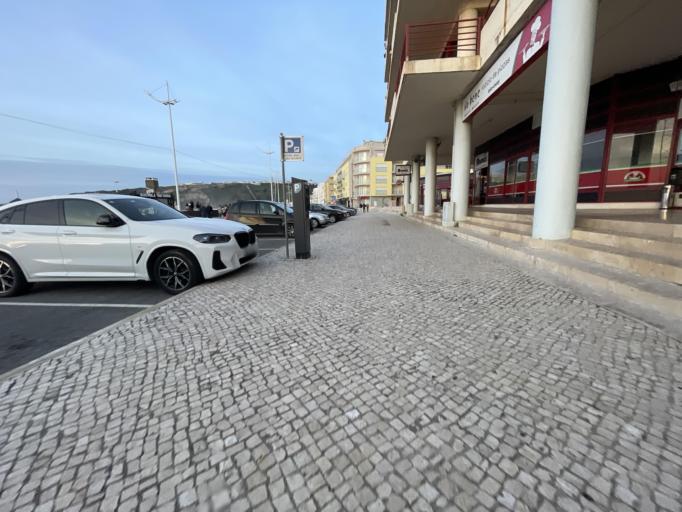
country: PT
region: Leiria
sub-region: Nazare
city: Nazare
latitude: 39.5929
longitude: -9.0727
